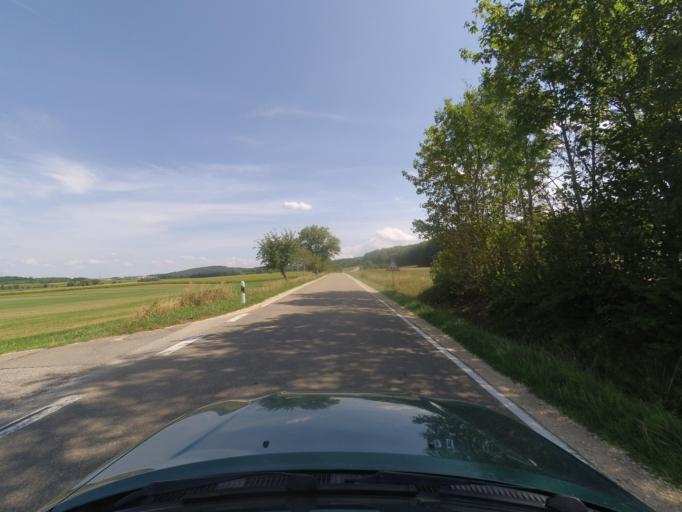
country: DE
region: Bavaria
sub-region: Regierungsbezirk Mittelfranken
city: Ettenstatt
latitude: 49.0756
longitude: 11.0659
